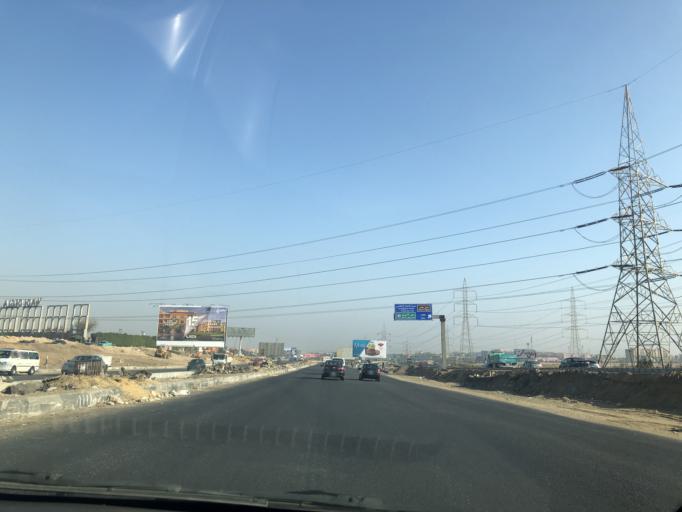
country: EG
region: Al Jizah
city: Madinat Sittah Uktubar
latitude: 29.9733
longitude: 31.0037
